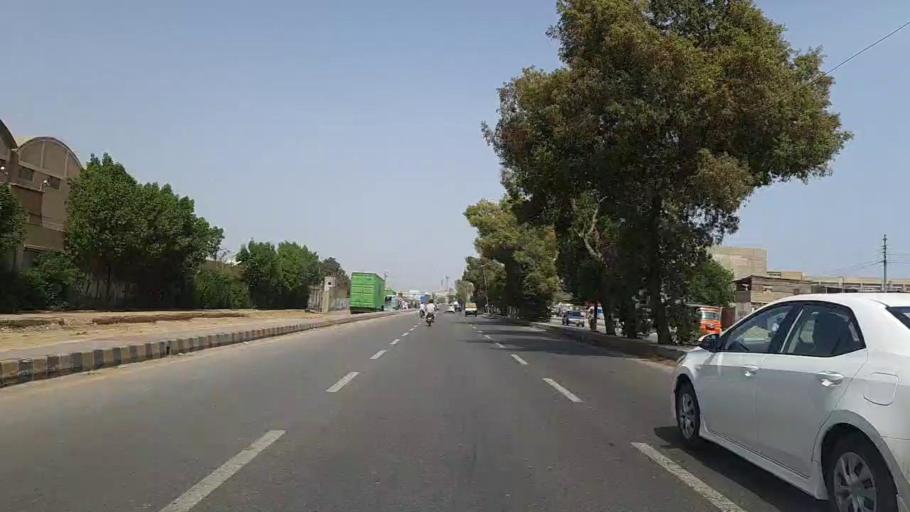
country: PK
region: Sindh
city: Malir Cantonment
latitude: 24.8544
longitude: 67.2365
